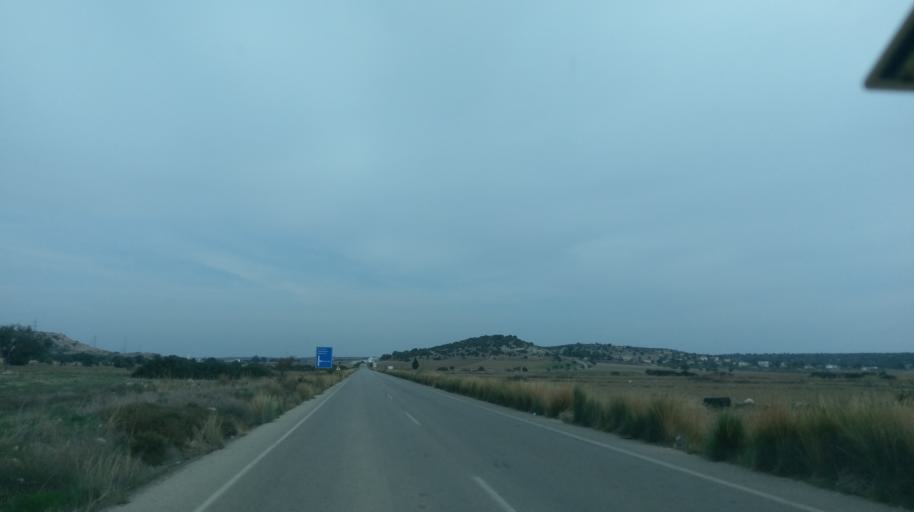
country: CY
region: Ammochostos
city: Leonarisso
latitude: 35.3956
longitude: 34.0640
